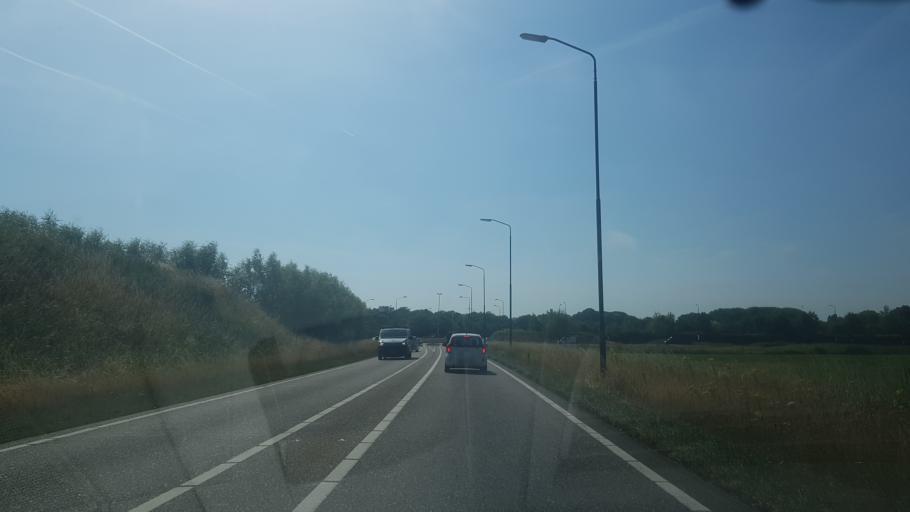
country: NL
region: North Brabant
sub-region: Gemeente Laarbeek
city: Aarle-Rixtel
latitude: 51.5519
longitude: 5.6228
